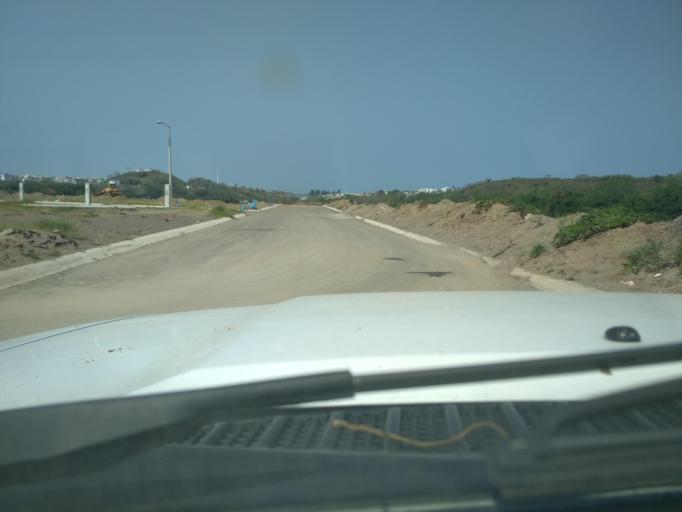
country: MX
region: Veracruz
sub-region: Veracruz
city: Lomas de Rio Medio Cuatro
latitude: 19.1905
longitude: -96.2056
